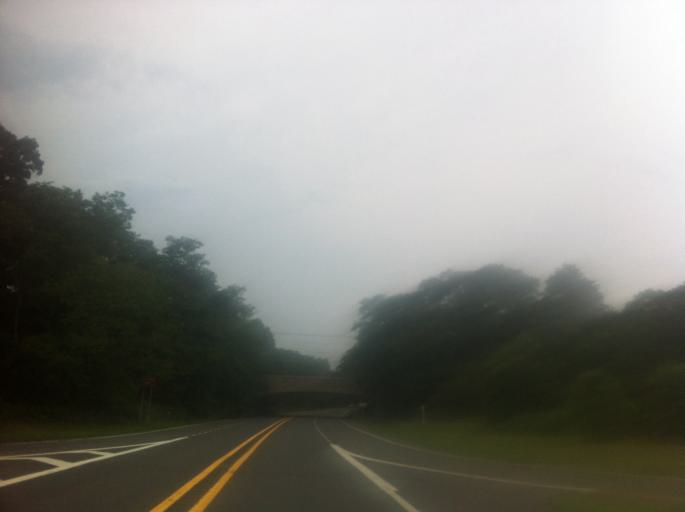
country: US
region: New York
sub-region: Nassau County
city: North Massapequa
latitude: 40.7212
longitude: -73.4631
